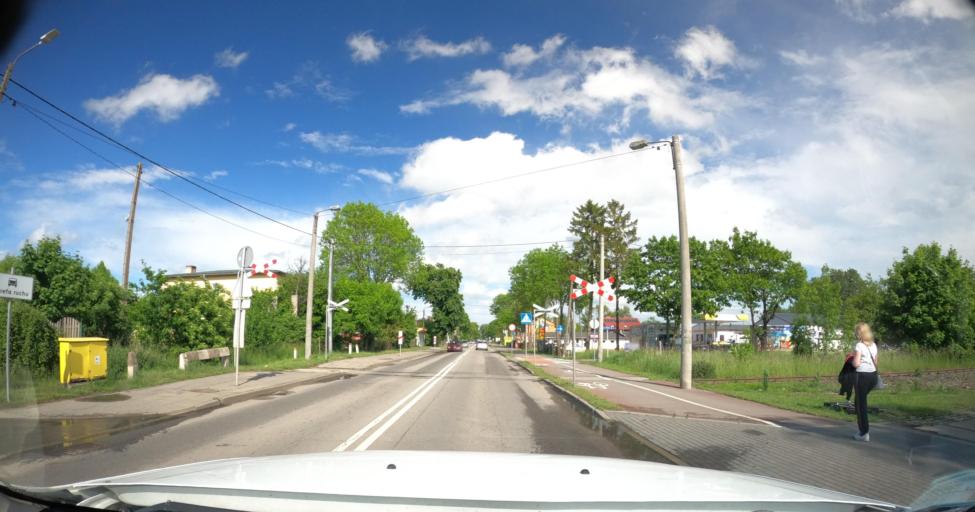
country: PL
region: Pomeranian Voivodeship
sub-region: Powiat nowodworski
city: Nowy Dwor Gdanski
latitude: 54.2085
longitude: 19.1237
